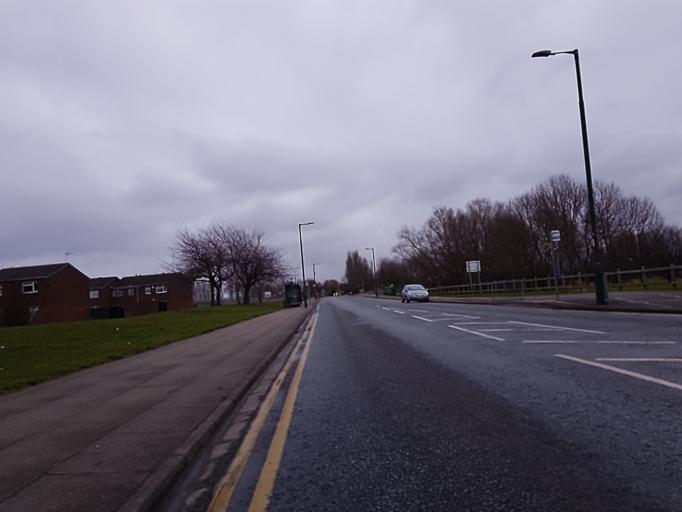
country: GB
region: England
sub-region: North East Lincolnshire
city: Great Coates
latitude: 53.5705
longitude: -0.1188
